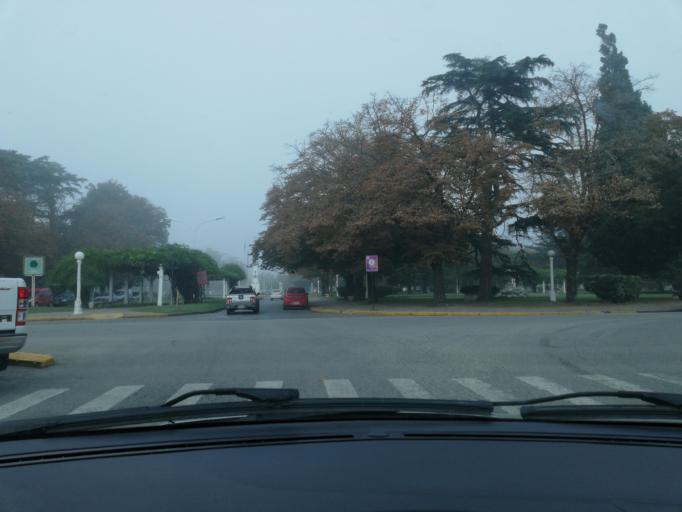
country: AR
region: Buenos Aires
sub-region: Partido de Balcarce
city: Balcarce
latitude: -37.8454
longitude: -58.2544
